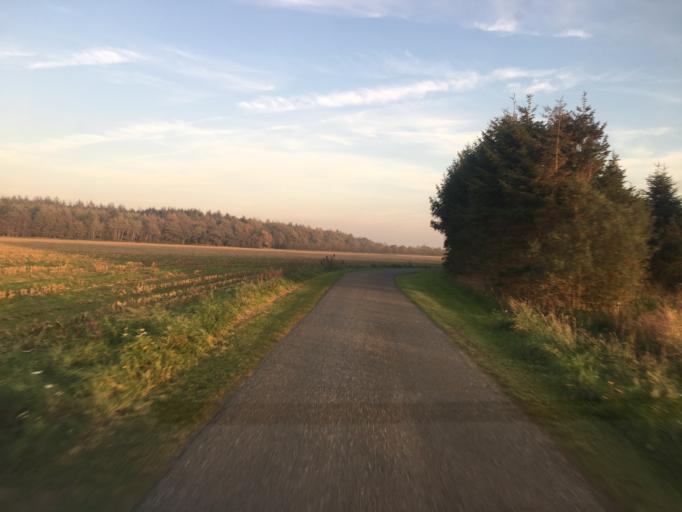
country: DK
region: South Denmark
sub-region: Tonder Kommune
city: Toftlund
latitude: 55.0323
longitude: 9.1197
